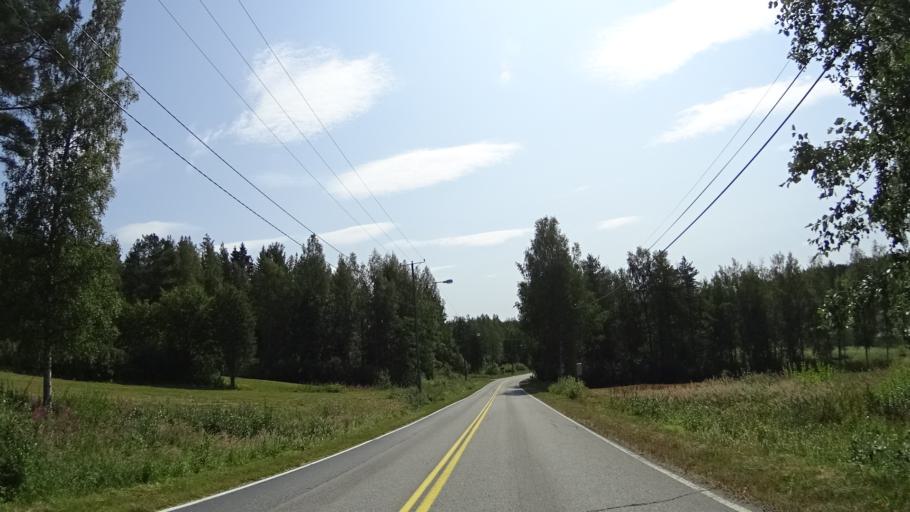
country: FI
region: Pirkanmaa
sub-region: Ylae-Pirkanmaa
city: Maenttae
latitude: 61.8999
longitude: 24.7926
